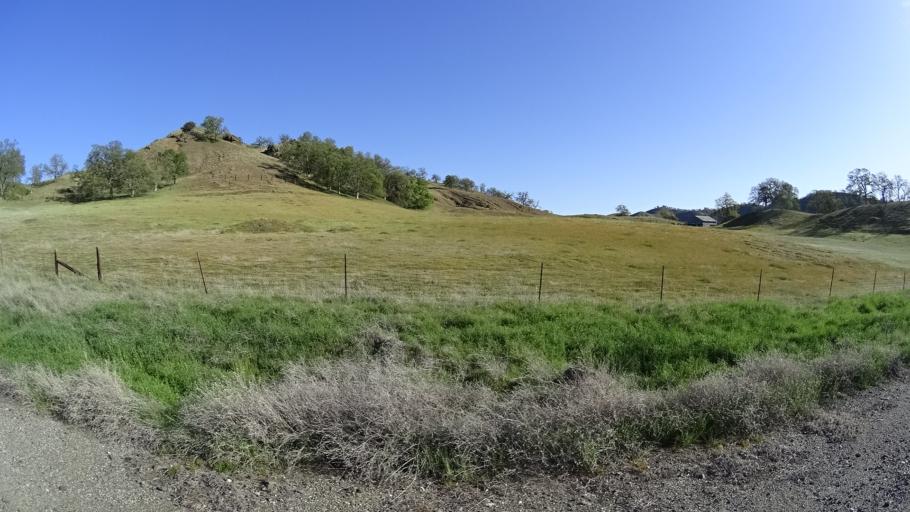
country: US
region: California
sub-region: Tehama County
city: Rancho Tehama Reserve
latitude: 39.7923
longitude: -122.5242
